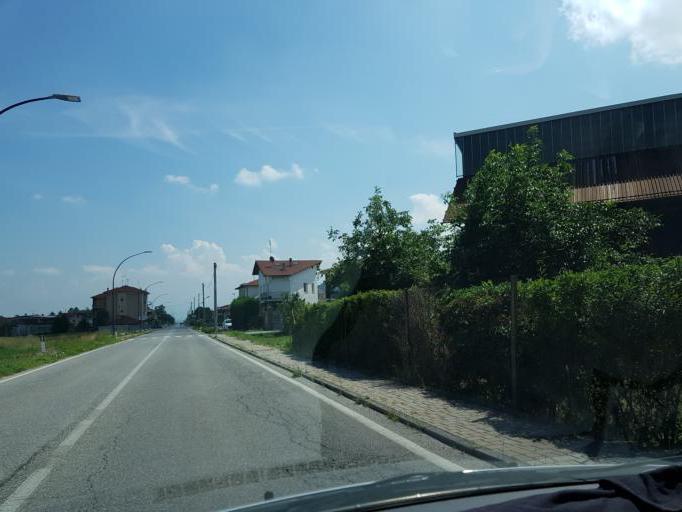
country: IT
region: Piedmont
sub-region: Provincia di Cuneo
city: Dronero
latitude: 44.4585
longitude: 7.3769
